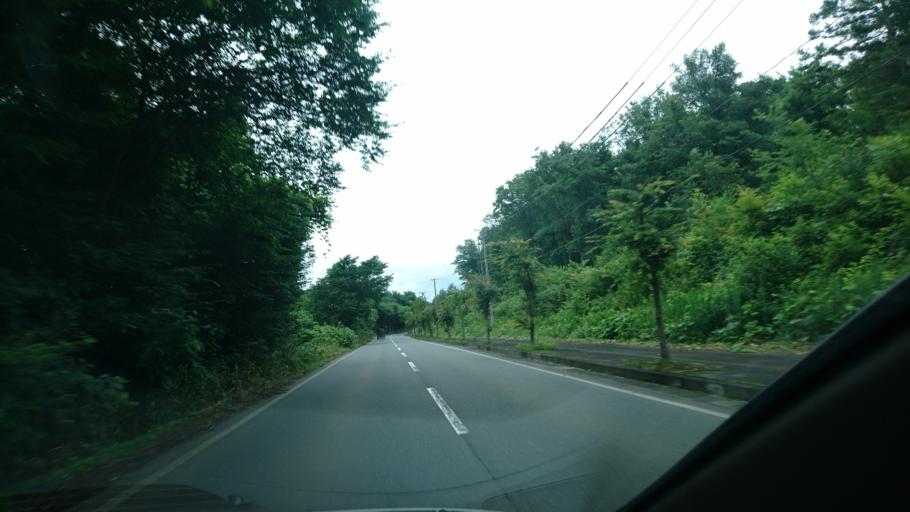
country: JP
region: Iwate
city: Mizusawa
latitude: 39.2101
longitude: 141.1743
